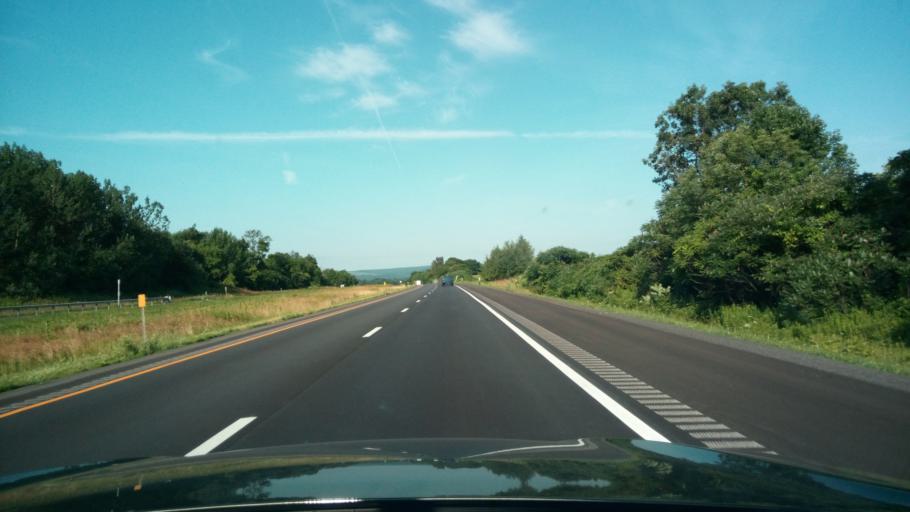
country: US
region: New York
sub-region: Steuben County
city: Wayland
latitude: 42.5340
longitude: -77.6355
